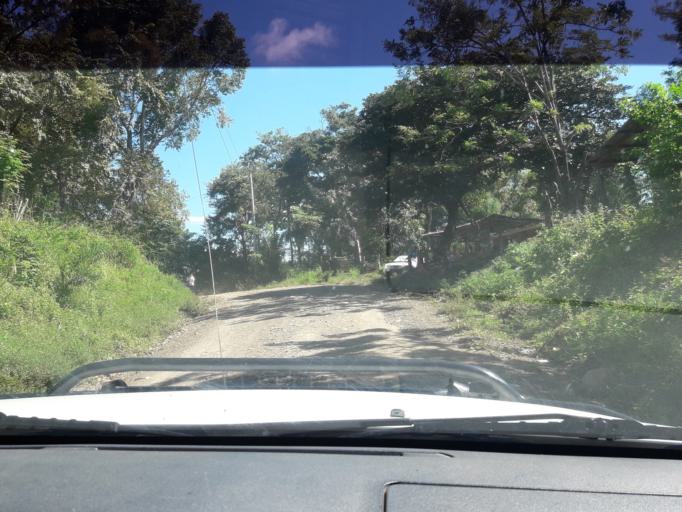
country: NI
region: Rivas
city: Cardenas
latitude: 11.2226
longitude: -85.6499
